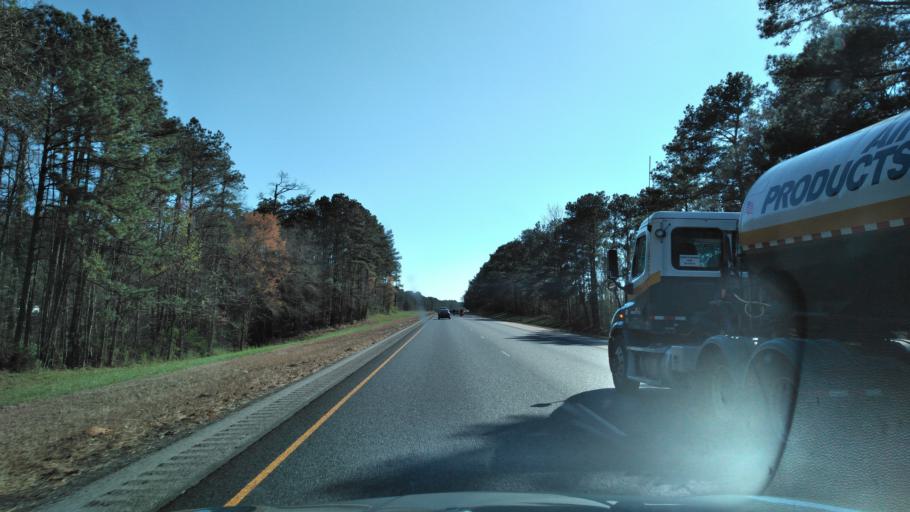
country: US
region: Alabama
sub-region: Butler County
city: Georgiana
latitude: 31.7491
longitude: -86.7092
